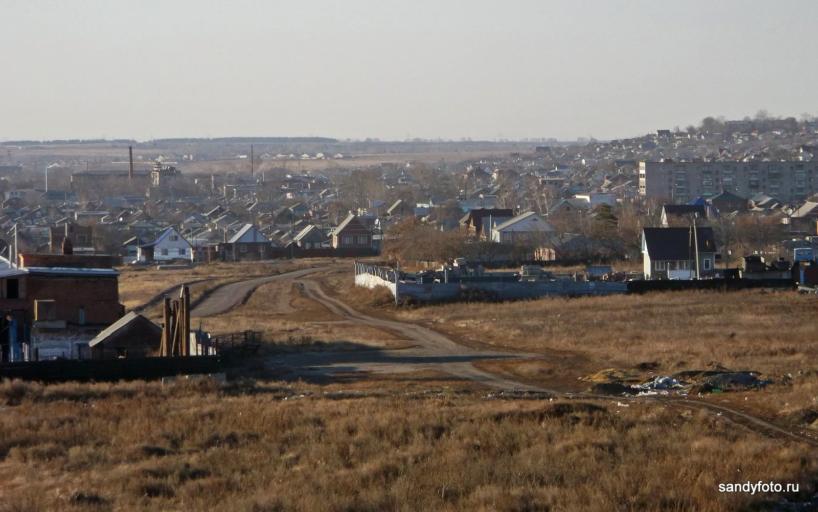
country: RU
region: Chelyabinsk
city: Troitsk
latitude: 54.0955
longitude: 61.6102
